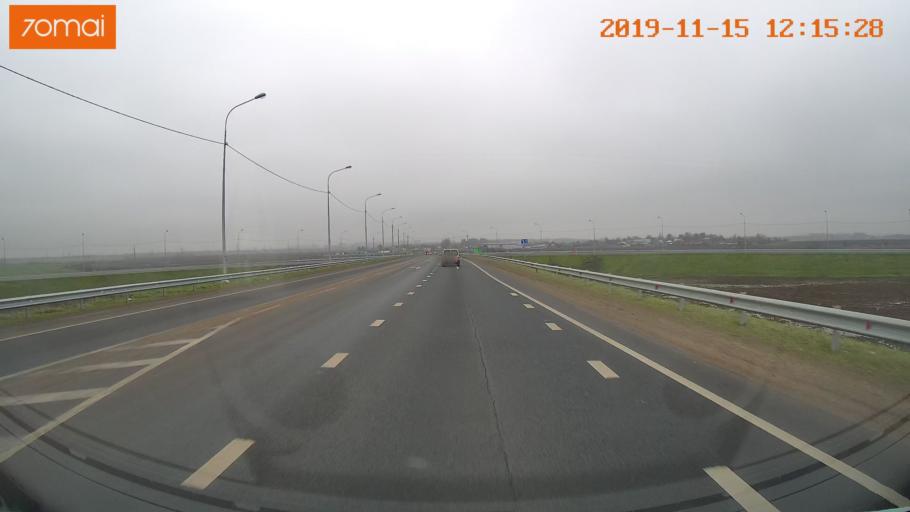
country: RU
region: Vologda
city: Vologda
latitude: 59.1593
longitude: 39.8136
